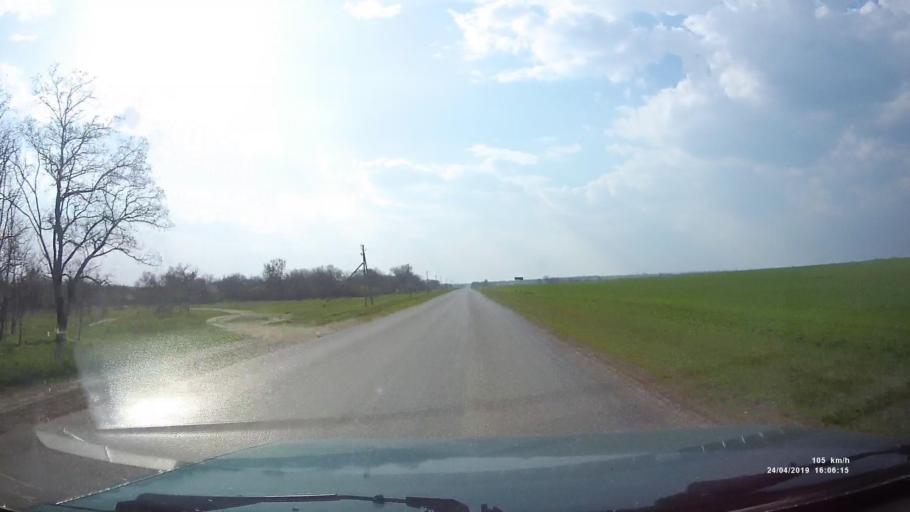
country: RU
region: Rostov
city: Sovetskoye
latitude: 46.6855
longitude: 42.3530
